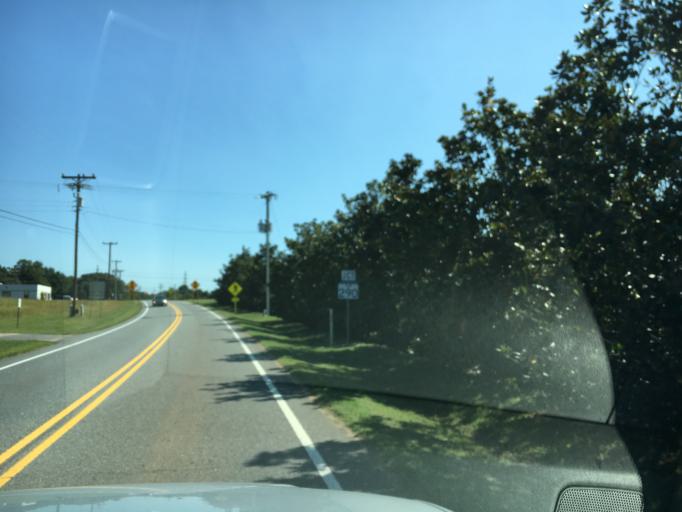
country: US
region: South Carolina
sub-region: Spartanburg County
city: Wellford
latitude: 34.8938
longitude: -82.0899
